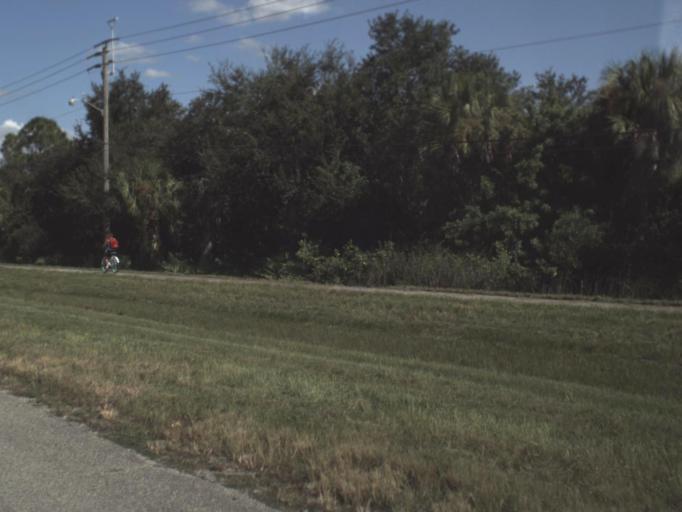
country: US
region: Florida
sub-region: Sarasota County
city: North Port
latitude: 26.9972
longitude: -82.1918
